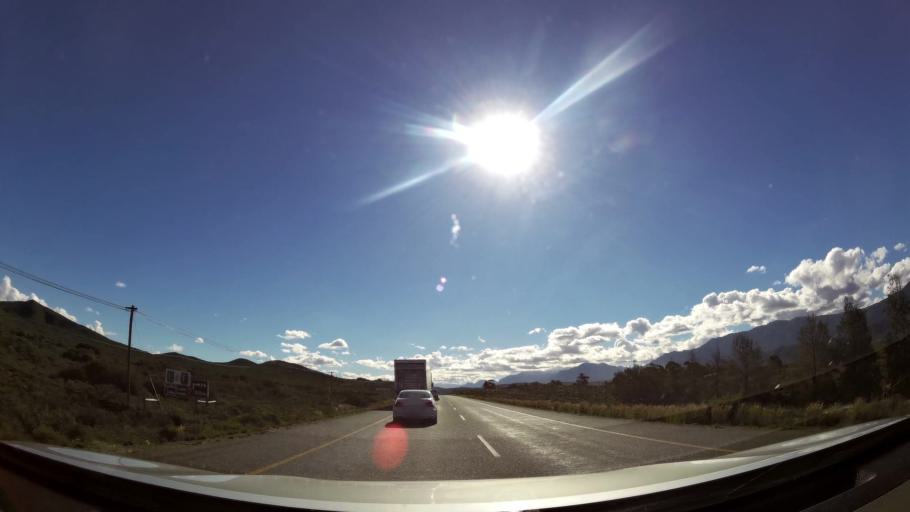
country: ZA
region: Western Cape
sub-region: Cape Winelands District Municipality
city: Worcester
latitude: -33.7652
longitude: 19.7438
